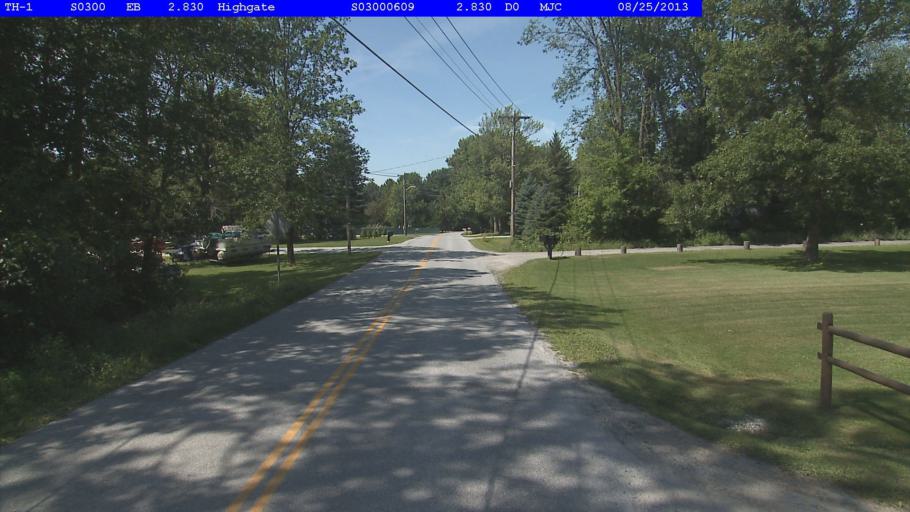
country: US
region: Vermont
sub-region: Franklin County
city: Swanton
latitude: 44.9631
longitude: -73.0974
